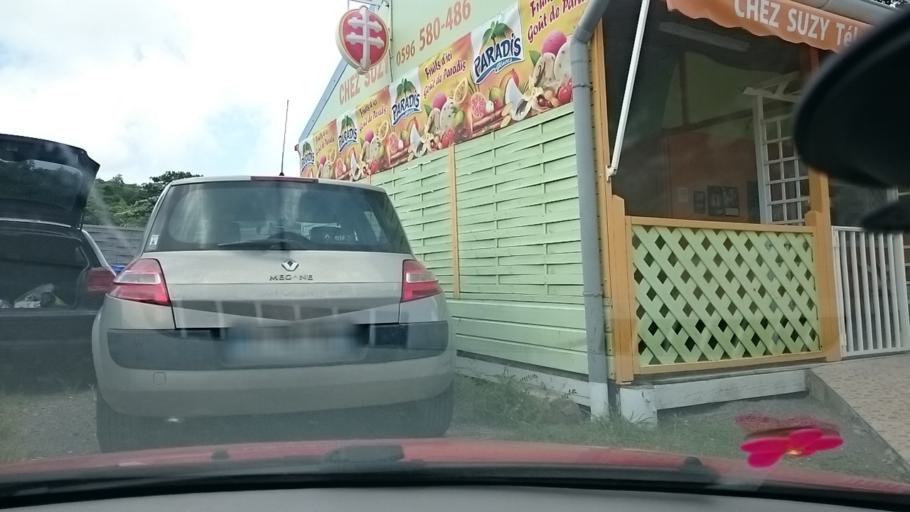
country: MQ
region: Martinique
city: Petite Riviere Salee
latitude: 14.7578
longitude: -60.9224
